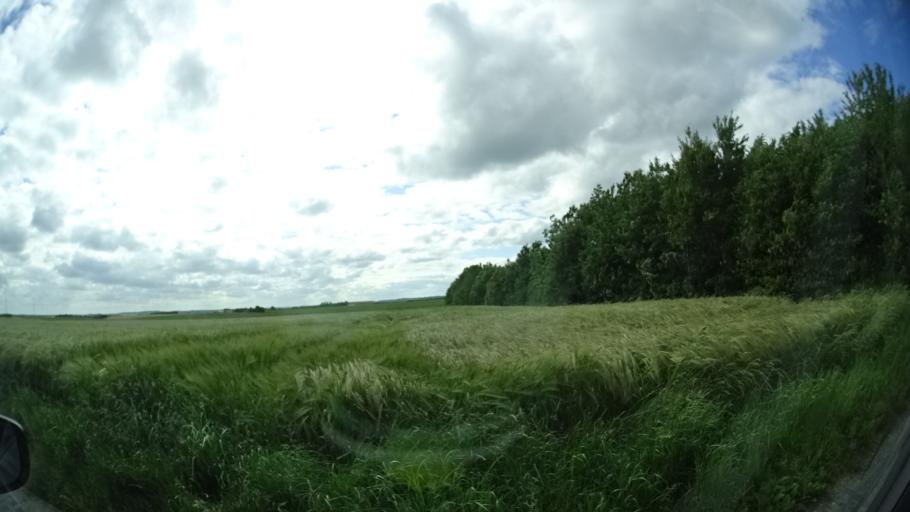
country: DK
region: Central Jutland
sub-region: Norddjurs Kommune
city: Grenaa
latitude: 56.4672
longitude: 10.7149
